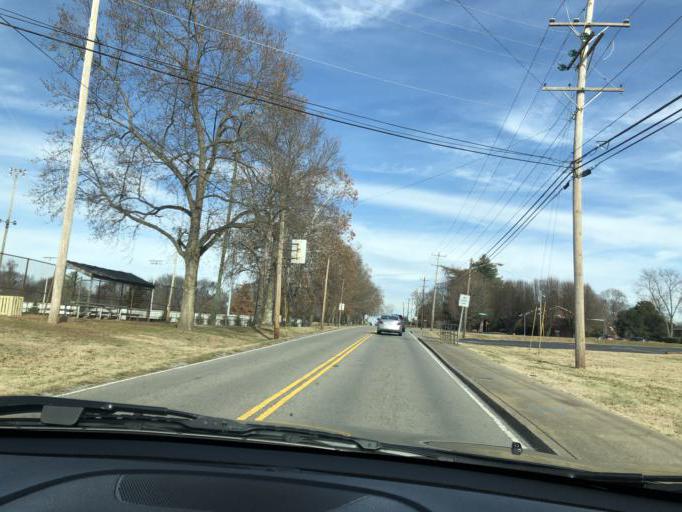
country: US
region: Tennessee
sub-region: Davidson County
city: Lakewood
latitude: 36.1863
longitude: -86.6759
